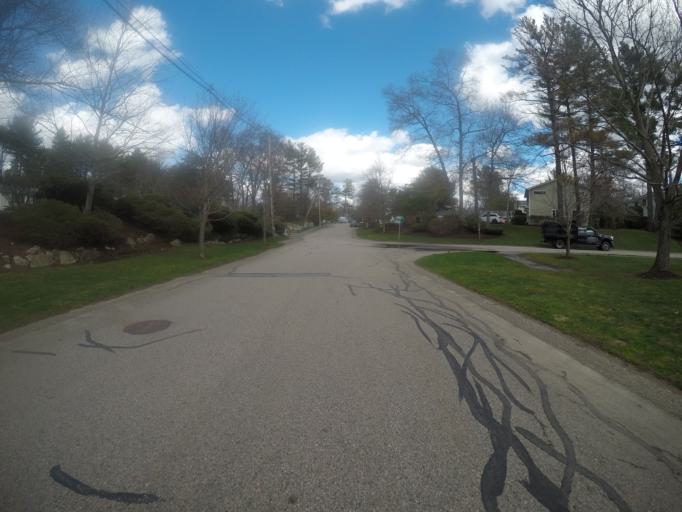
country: US
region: Massachusetts
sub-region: Bristol County
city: Easton
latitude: 42.0373
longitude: -71.0769
